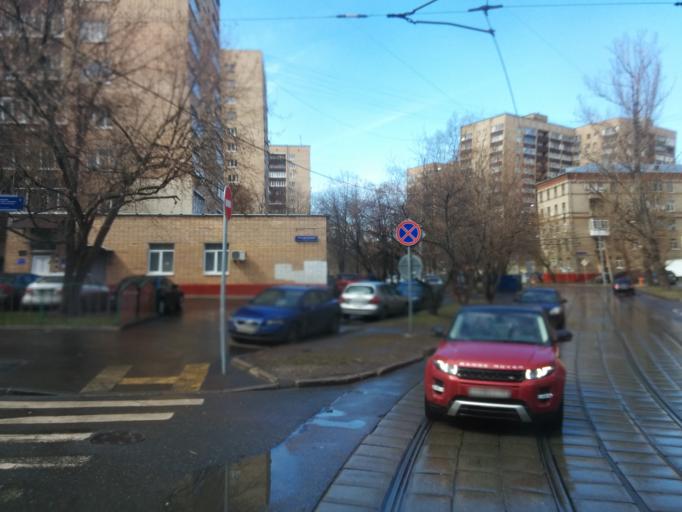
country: RU
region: Moscow
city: Mar'ina Roshcha
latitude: 55.7793
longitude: 37.6134
